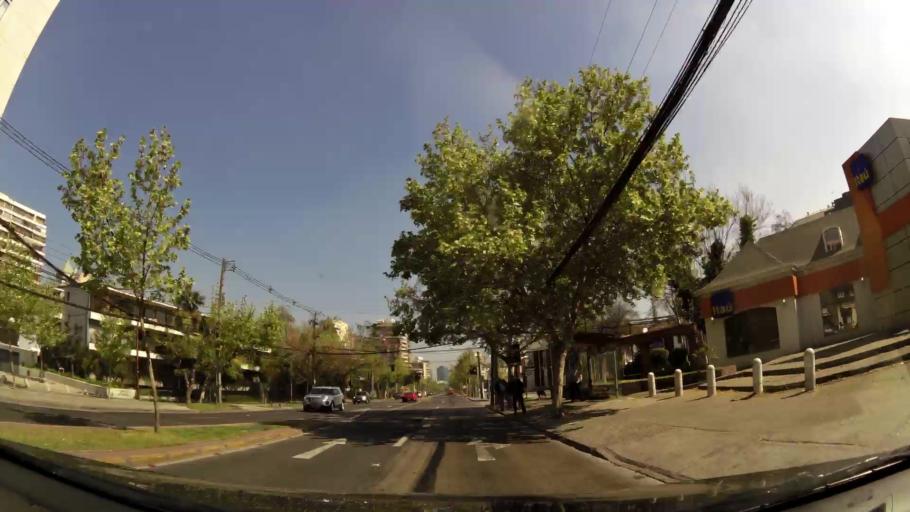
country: CL
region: Santiago Metropolitan
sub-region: Provincia de Santiago
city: Villa Presidente Frei, Nunoa, Santiago, Chile
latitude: -33.4037
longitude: -70.5959
